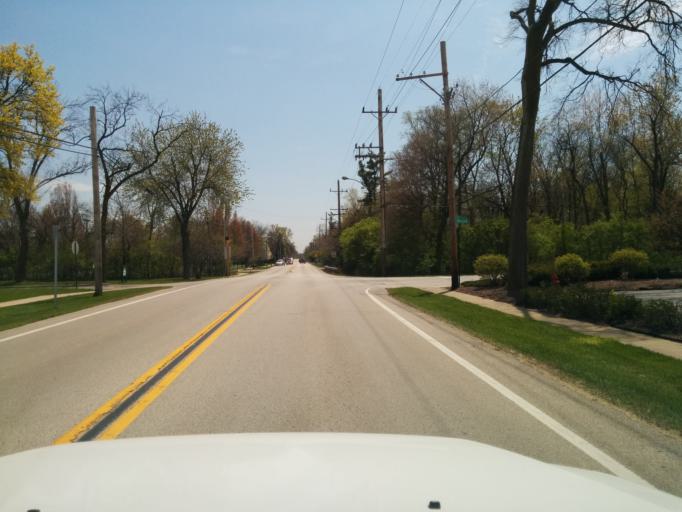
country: US
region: Illinois
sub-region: Cook County
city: Indian Head Park
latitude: 41.7540
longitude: -87.8964
